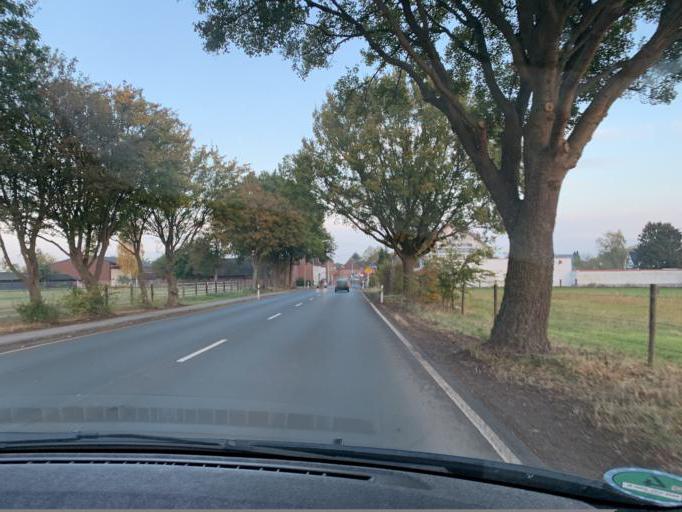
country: DE
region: North Rhine-Westphalia
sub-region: Regierungsbezirk Dusseldorf
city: Juchen
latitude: 51.1188
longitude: 6.4649
